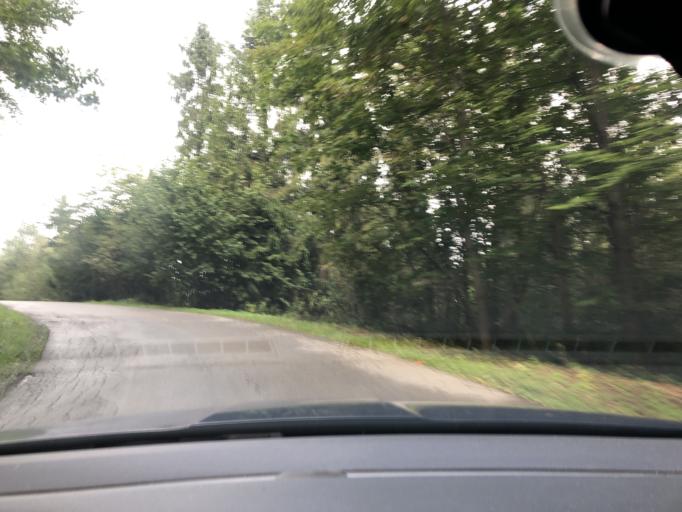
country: PL
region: Silesian Voivodeship
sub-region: Powiat zywiecki
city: Slemien
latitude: 49.7221
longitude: 19.4166
